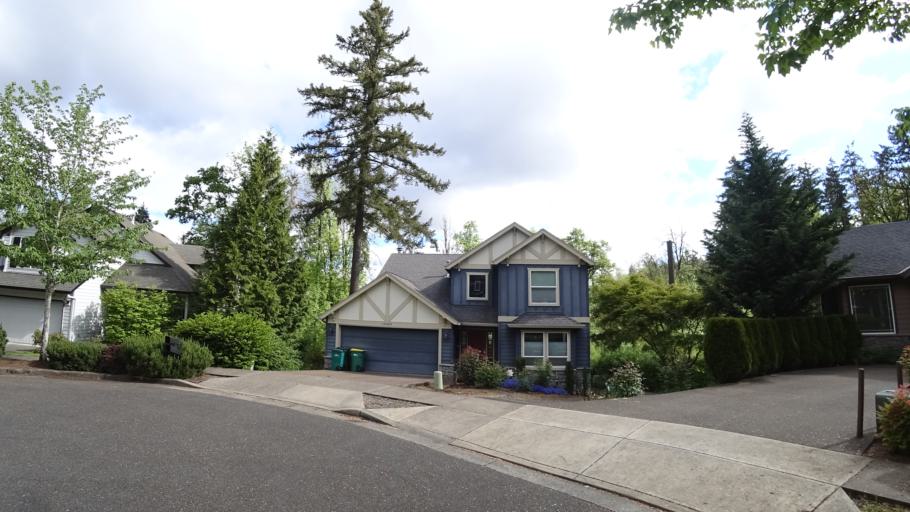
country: US
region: Oregon
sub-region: Washington County
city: Beaverton
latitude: 45.4644
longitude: -122.8359
